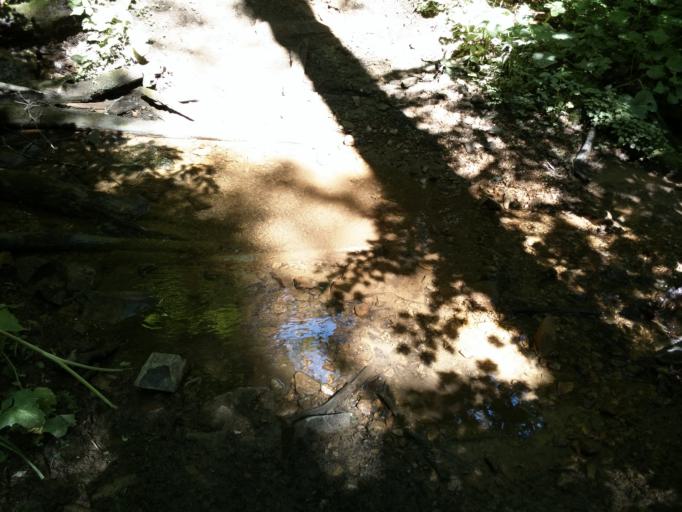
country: RU
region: Primorskiy
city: Trudovoye
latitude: 43.2011
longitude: 132.0305
